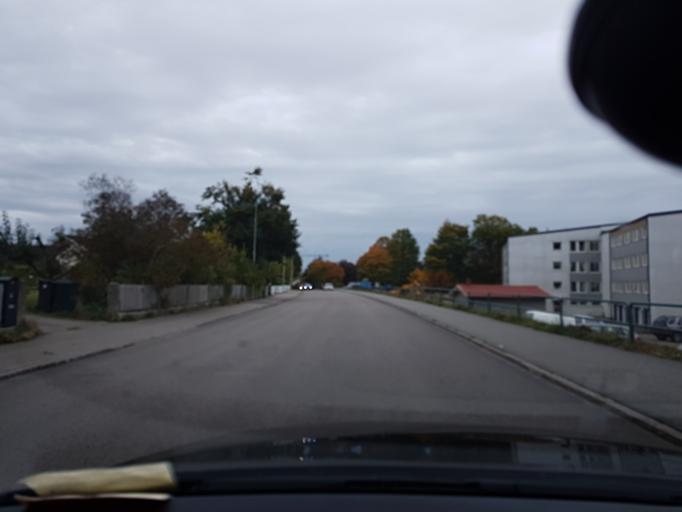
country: SE
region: Kronoberg
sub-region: Vaxjo Kommun
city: Vaexjoe
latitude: 56.8933
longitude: 14.8022
